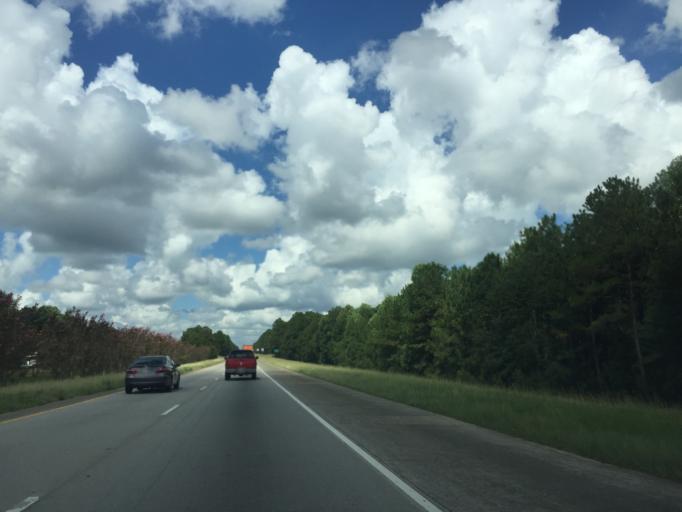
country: US
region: Georgia
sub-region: Candler County
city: Metter
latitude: 32.3821
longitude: -82.2229
